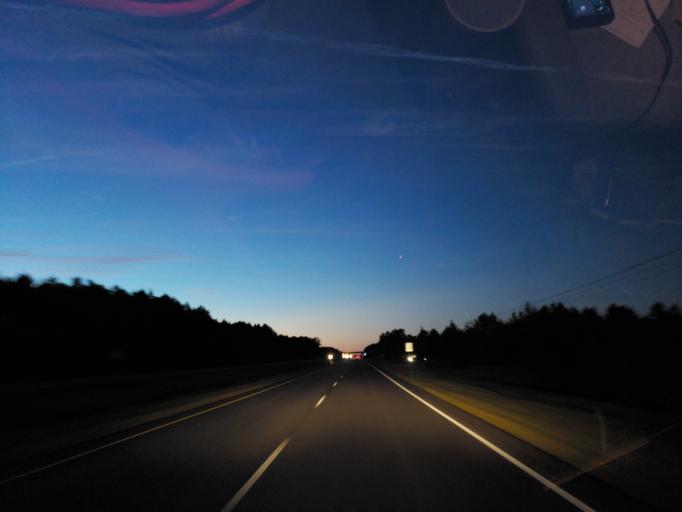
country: US
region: Mississippi
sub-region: Clarke County
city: Quitman
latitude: 32.0702
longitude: -88.6846
